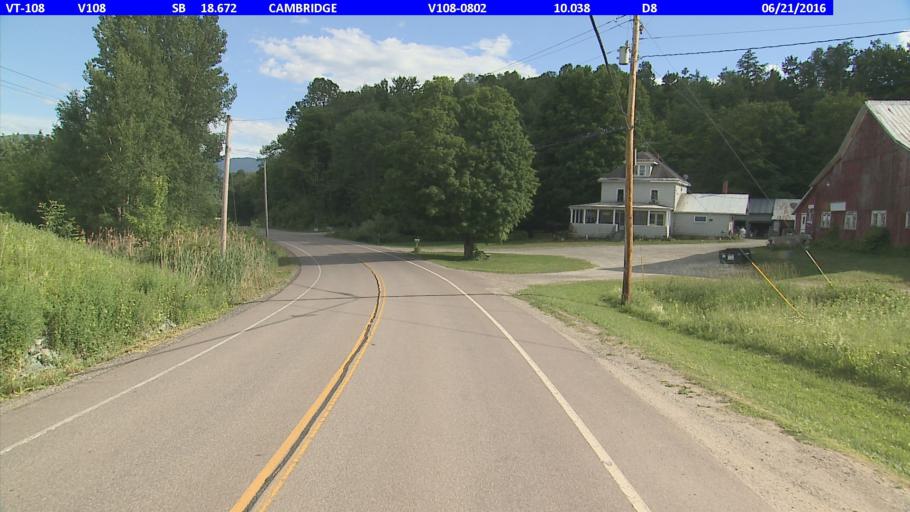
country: US
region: Vermont
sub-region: Lamoille County
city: Johnson
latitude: 44.6607
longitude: -72.8307
